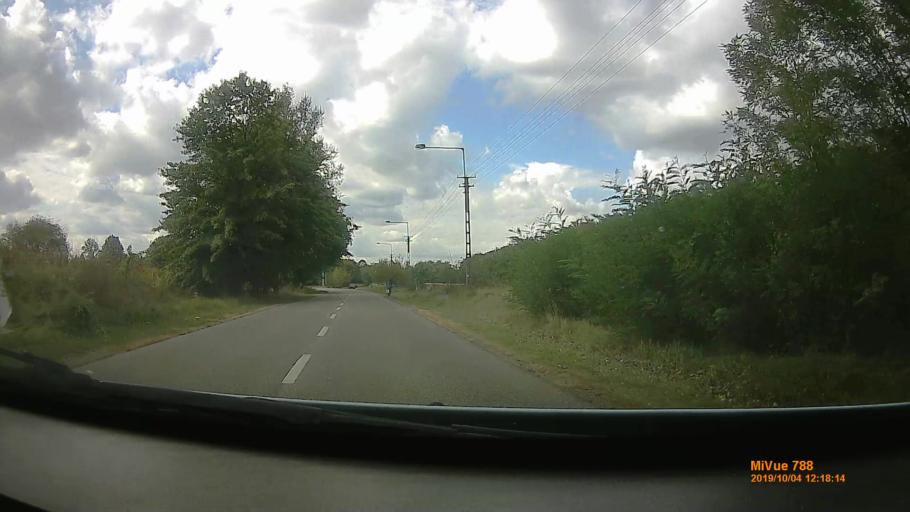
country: HU
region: Szabolcs-Szatmar-Bereg
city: Kotaj
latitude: 48.0254
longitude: 21.6850
